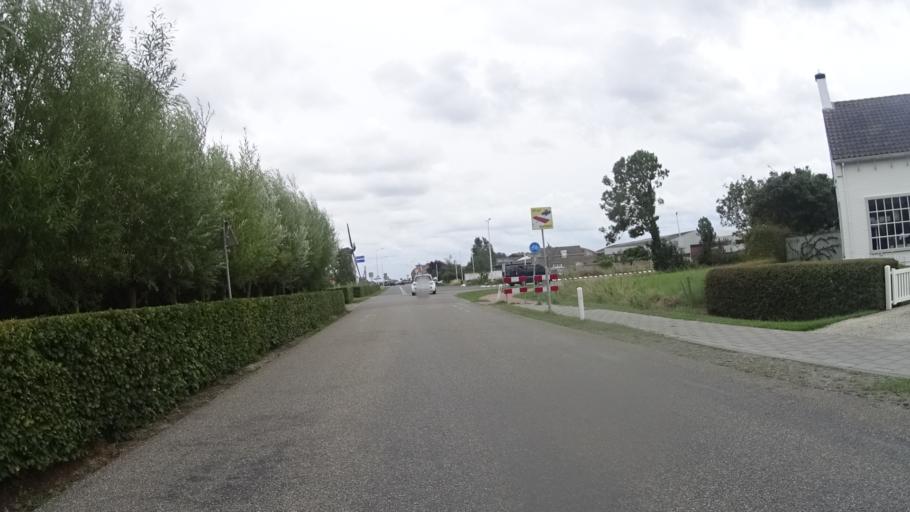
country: NL
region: Zeeland
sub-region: Gemeente Sluis
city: Sluis
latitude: 51.3669
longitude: 3.4108
